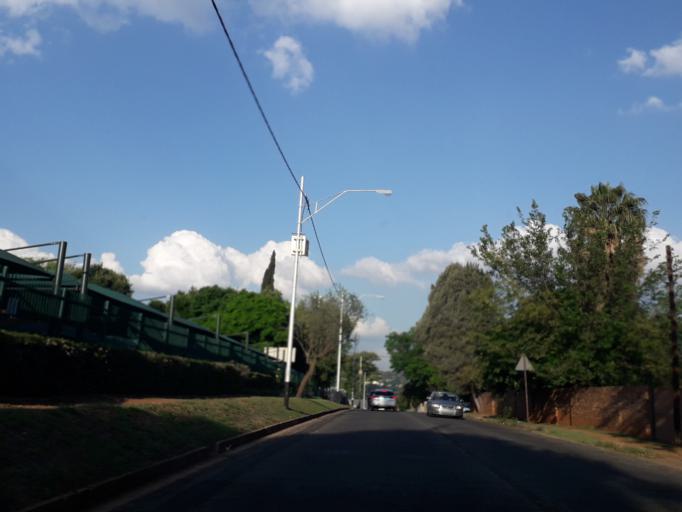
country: ZA
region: Gauteng
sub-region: City of Johannesburg Metropolitan Municipality
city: Johannesburg
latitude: -26.1377
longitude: 28.0036
